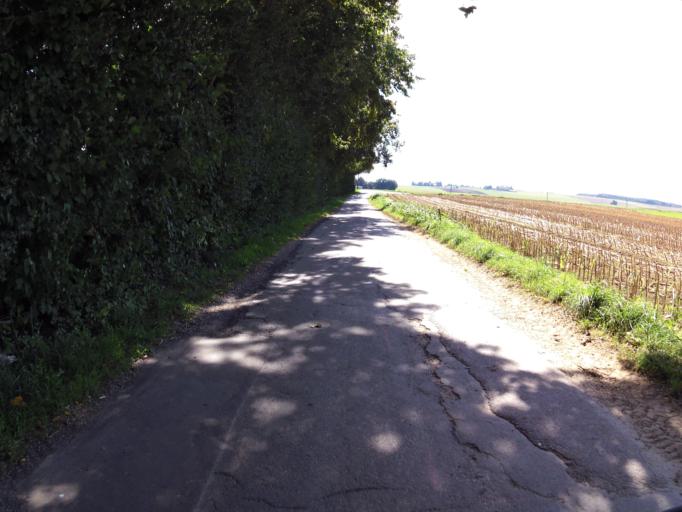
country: DE
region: Baden-Wuerttemberg
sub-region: Freiburg Region
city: Bad Durrheim
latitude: 47.9955
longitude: 8.5033
